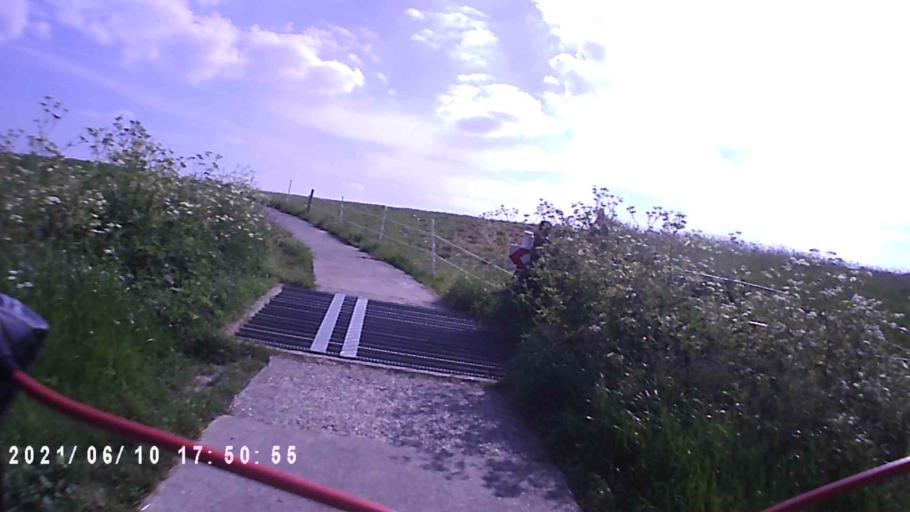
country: NL
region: Groningen
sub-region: Gemeente De Marne
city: Ulrum
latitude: 53.3315
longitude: 6.3128
